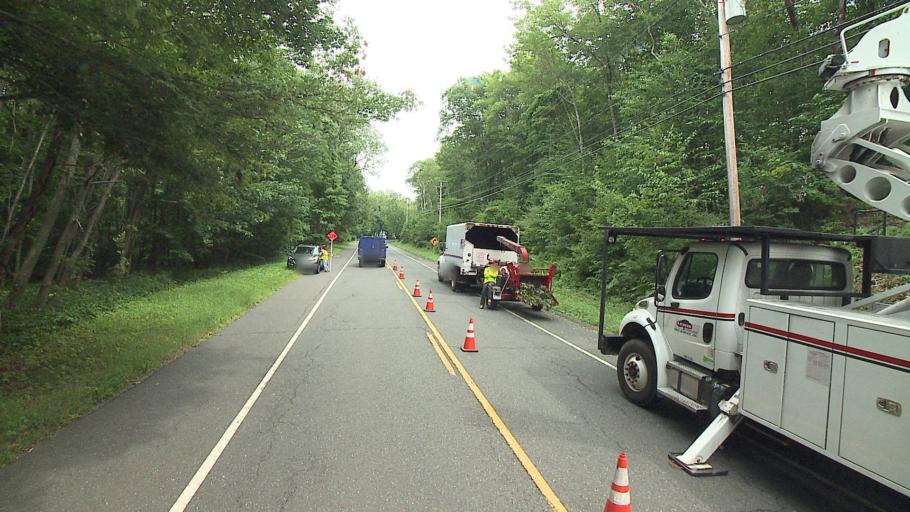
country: US
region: Connecticut
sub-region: Litchfield County
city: Woodbury
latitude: 41.5629
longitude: -73.2982
